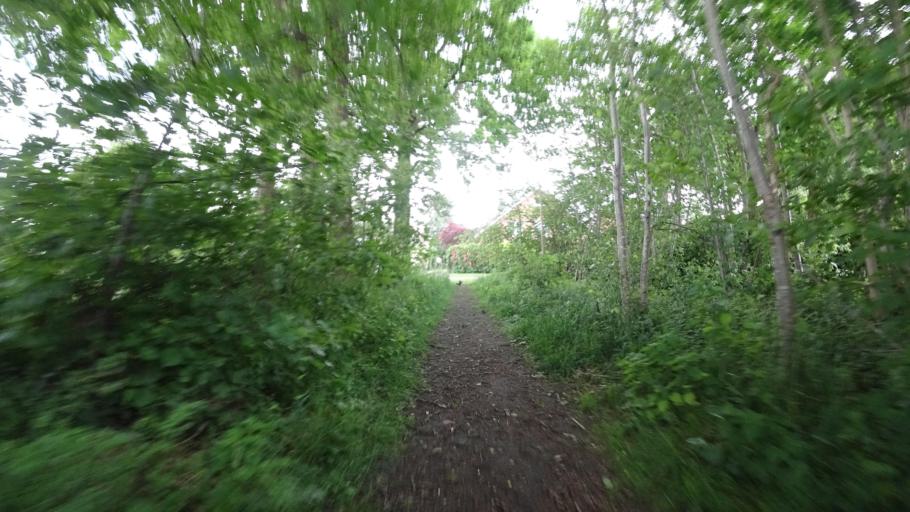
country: DE
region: North Rhine-Westphalia
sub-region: Regierungsbezirk Detmold
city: Guetersloh
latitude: 51.8939
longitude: 8.4353
